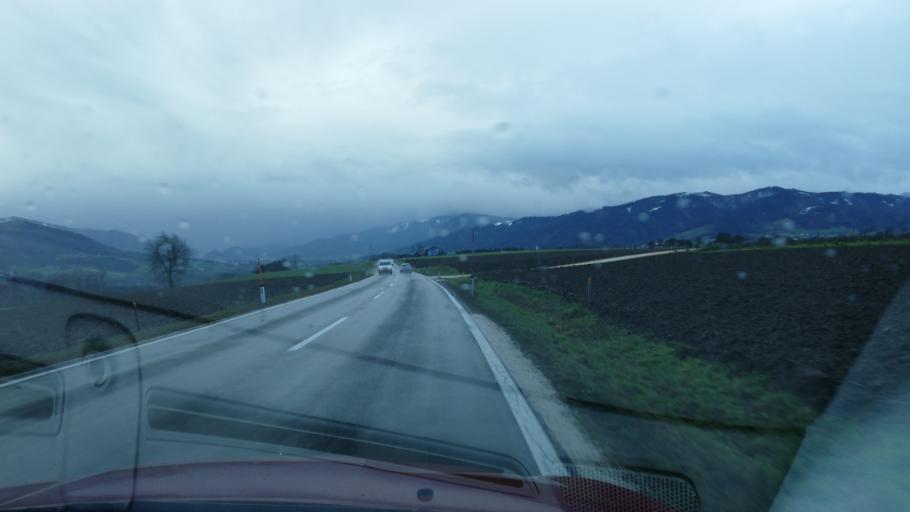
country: AT
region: Upper Austria
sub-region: Politischer Bezirk Kirchdorf an der Krems
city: Kremsmunster
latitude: 47.9726
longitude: 14.0781
